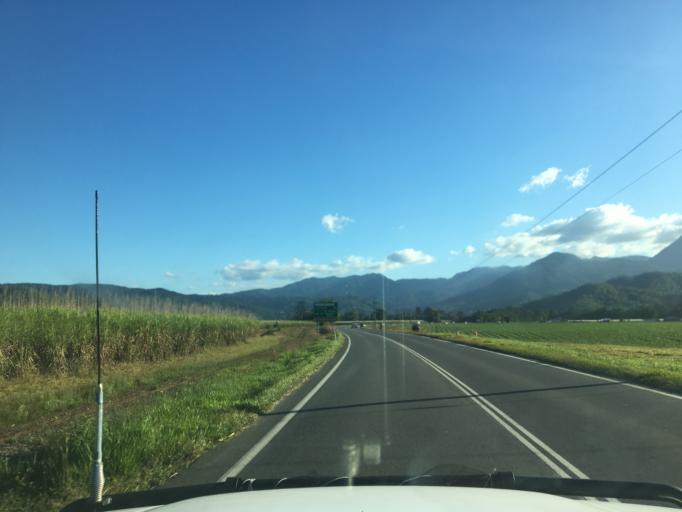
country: AU
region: Queensland
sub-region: Cairns
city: Port Douglas
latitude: -16.4799
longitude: 145.3931
